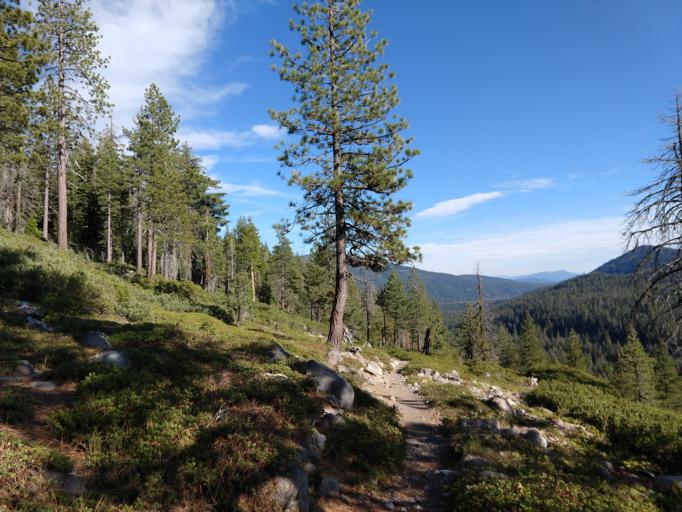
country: US
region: California
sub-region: Plumas County
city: Chester
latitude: 40.4460
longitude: -121.3984
